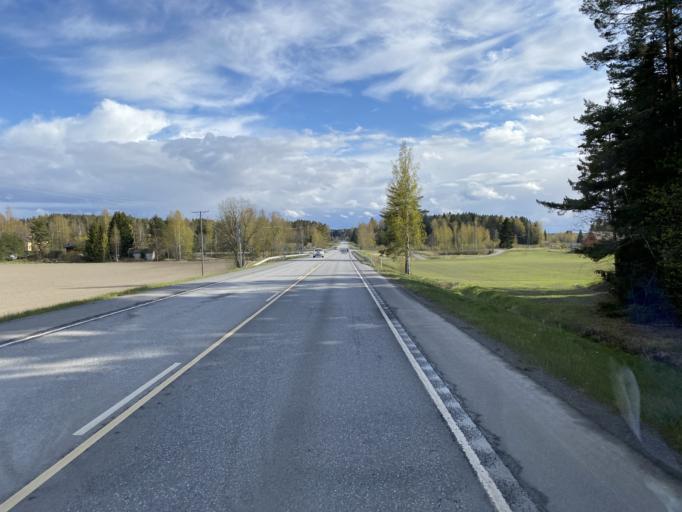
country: FI
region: Pirkanmaa
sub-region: Tampere
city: Lempaeaelae
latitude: 61.2689
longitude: 23.7464
